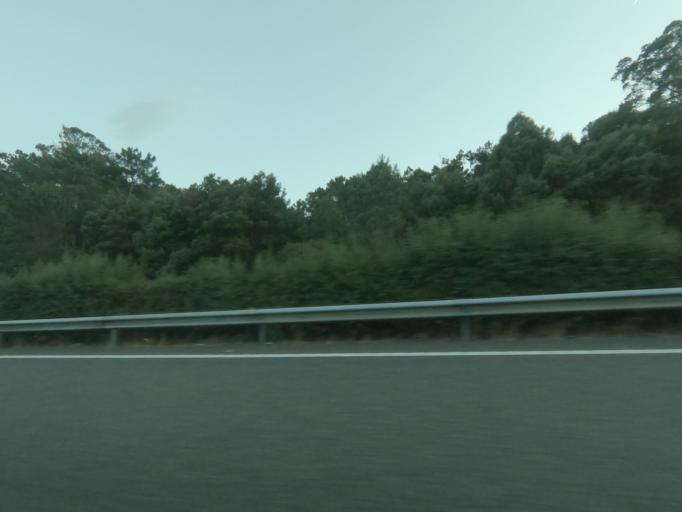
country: ES
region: Galicia
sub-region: Provincia de Pontevedra
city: Ponteareas
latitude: 42.1730
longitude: -8.5548
